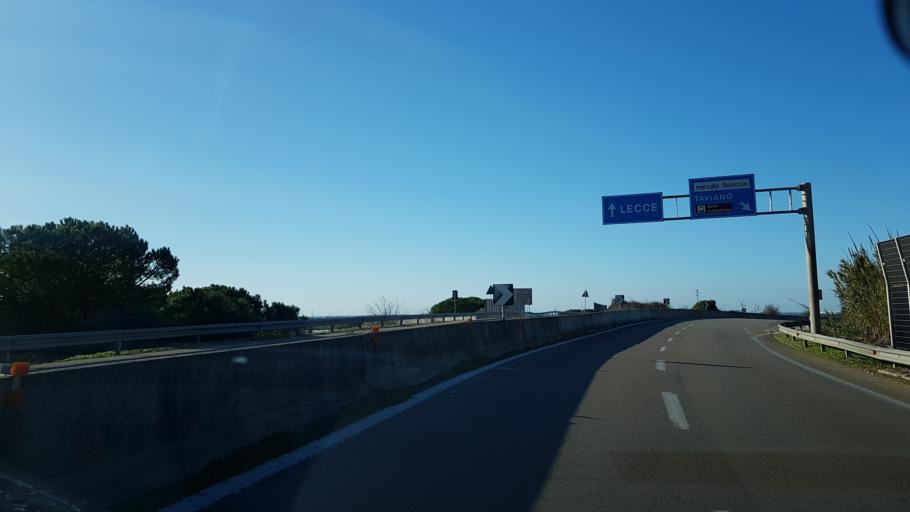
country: IT
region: Apulia
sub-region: Provincia di Lecce
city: Taviano
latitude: 40.0011
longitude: 18.0640
